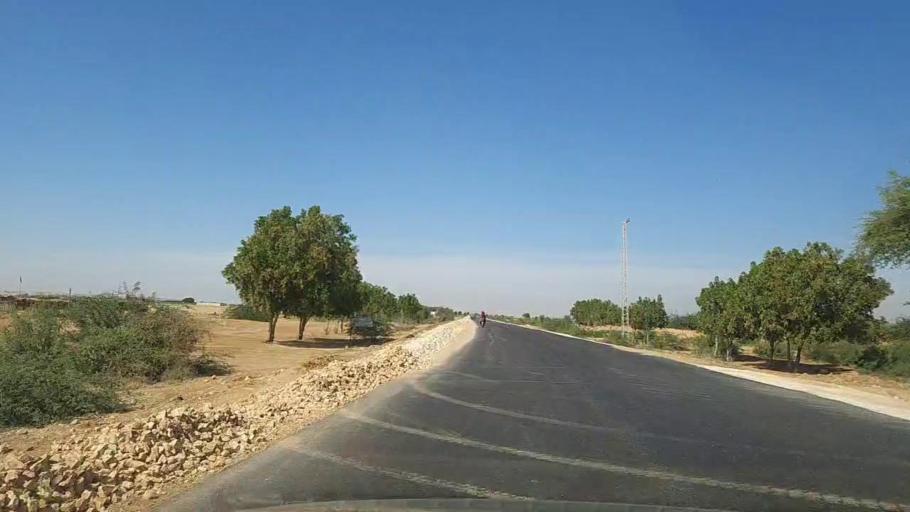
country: PK
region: Sindh
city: Kotri
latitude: 25.2514
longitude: 68.2273
